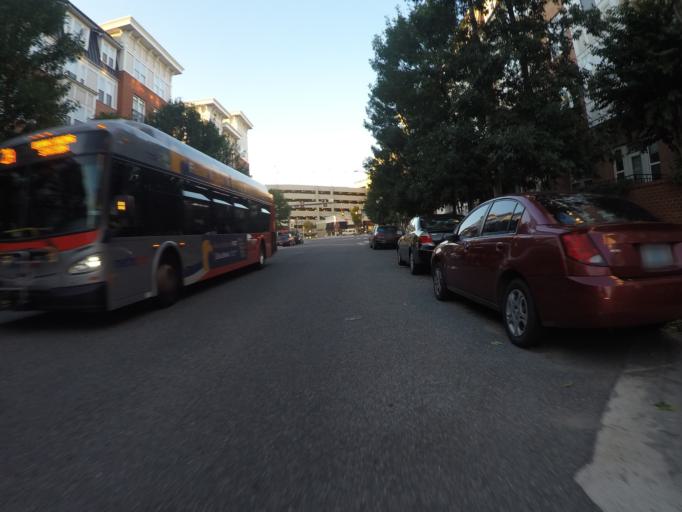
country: US
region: Virginia
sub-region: Fairfax County
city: Merrifield
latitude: 38.8800
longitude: -77.2307
